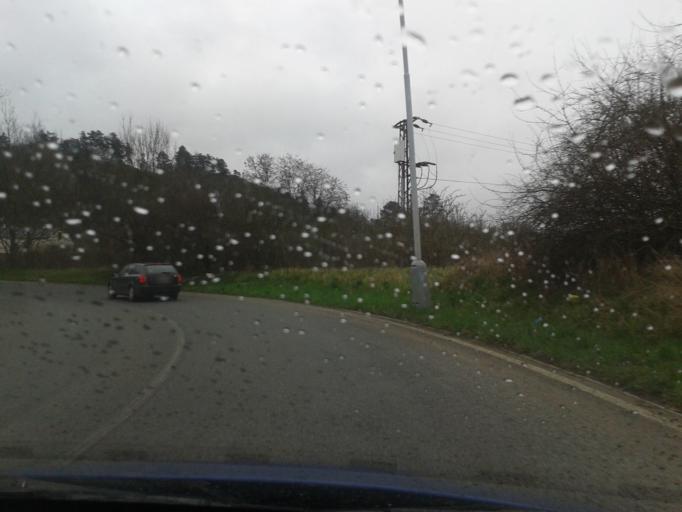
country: CZ
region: Central Bohemia
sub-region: Okres Beroun
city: Beroun
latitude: 49.9607
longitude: 14.0877
